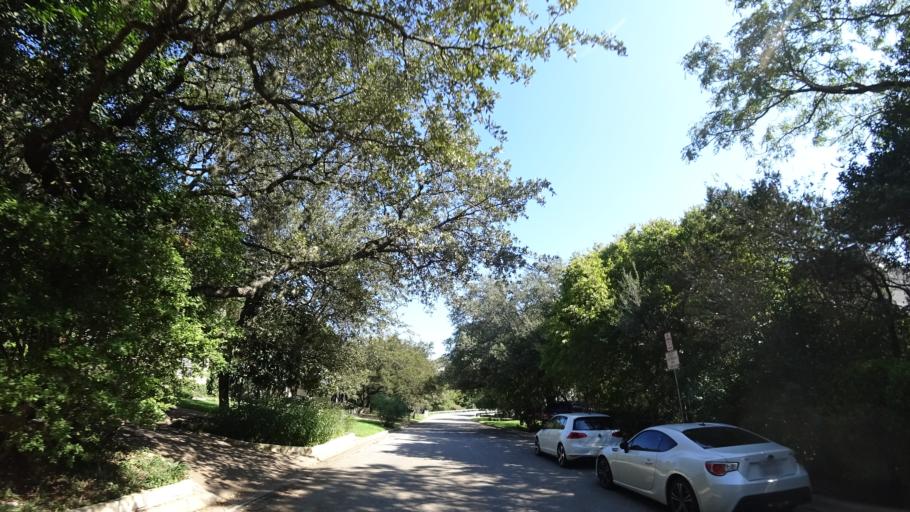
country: US
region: Texas
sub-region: Travis County
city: Rollingwood
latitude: 30.2751
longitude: -97.8098
